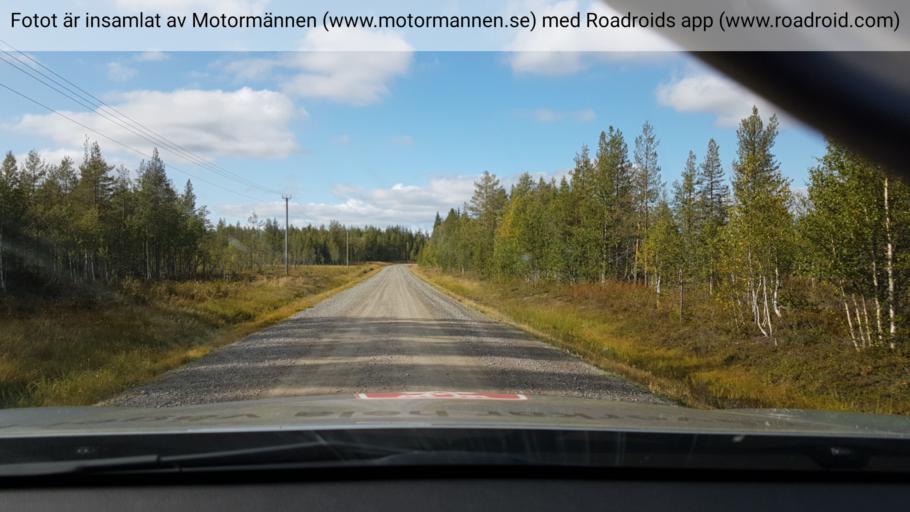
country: SE
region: Vaesterbotten
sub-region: Sorsele Kommun
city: Sorsele
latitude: 65.5110
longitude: 18.0212
